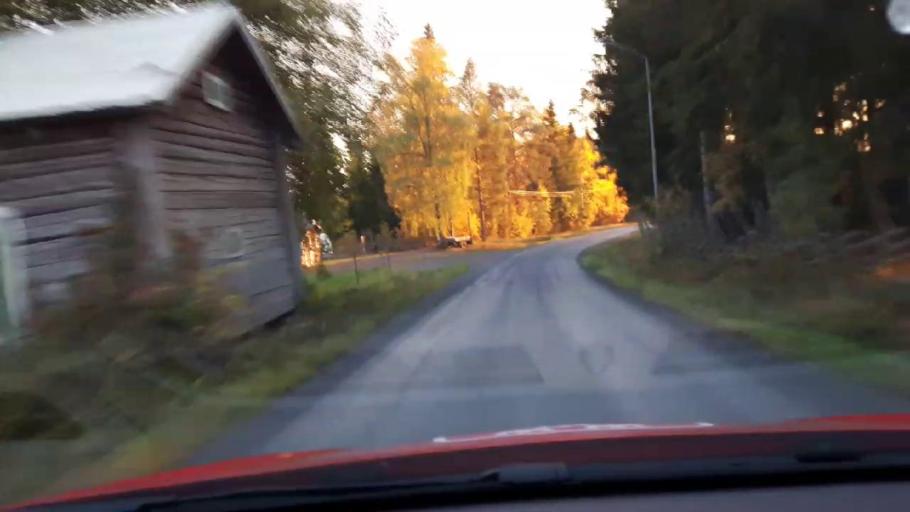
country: SE
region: Jaemtland
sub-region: OEstersunds Kommun
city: Lit
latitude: 63.2835
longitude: 14.7771
